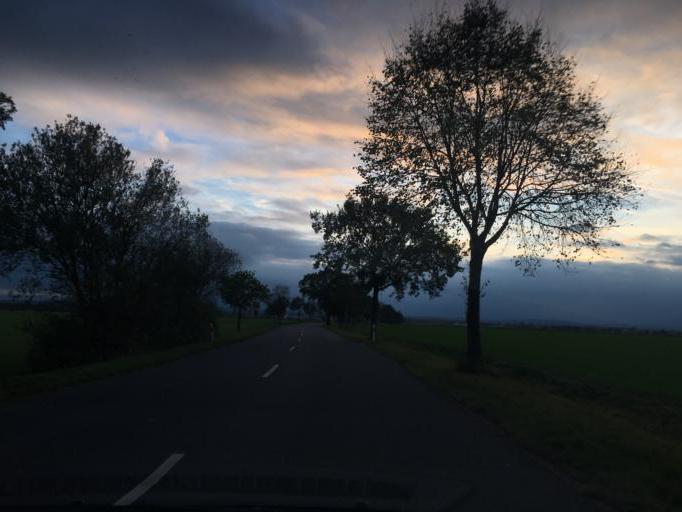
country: DE
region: North Rhine-Westphalia
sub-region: Regierungsbezirk Koln
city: Vettweiss
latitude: 50.7575
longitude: 6.6268
